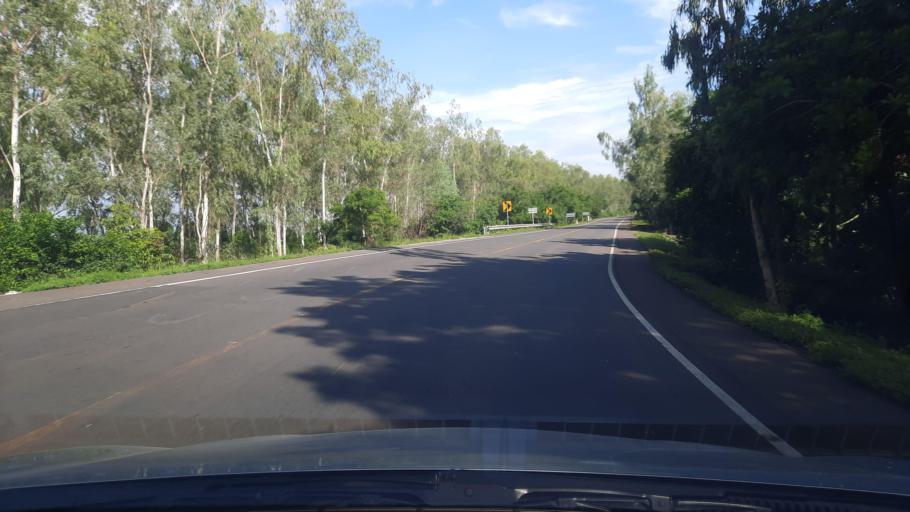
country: NI
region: Chinandega
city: Posoltega
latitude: 12.7343
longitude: -86.8817
